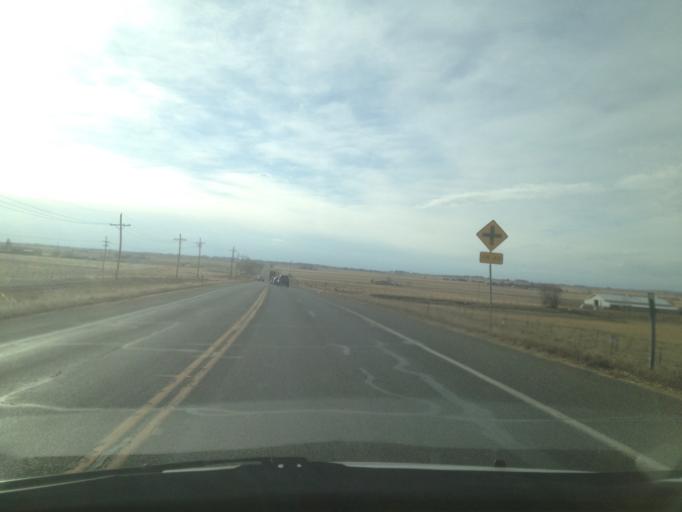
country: US
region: Colorado
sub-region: Weld County
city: Hudson
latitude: 40.0806
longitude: -104.6566
